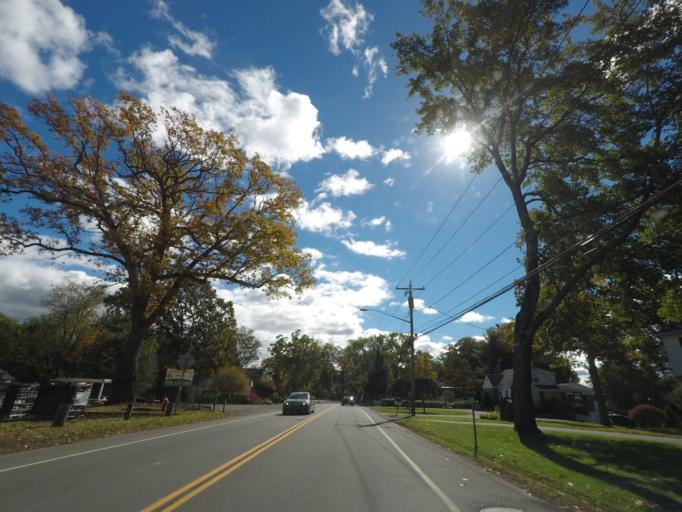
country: US
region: New York
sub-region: Albany County
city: Watervliet
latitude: 42.7258
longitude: -73.7271
